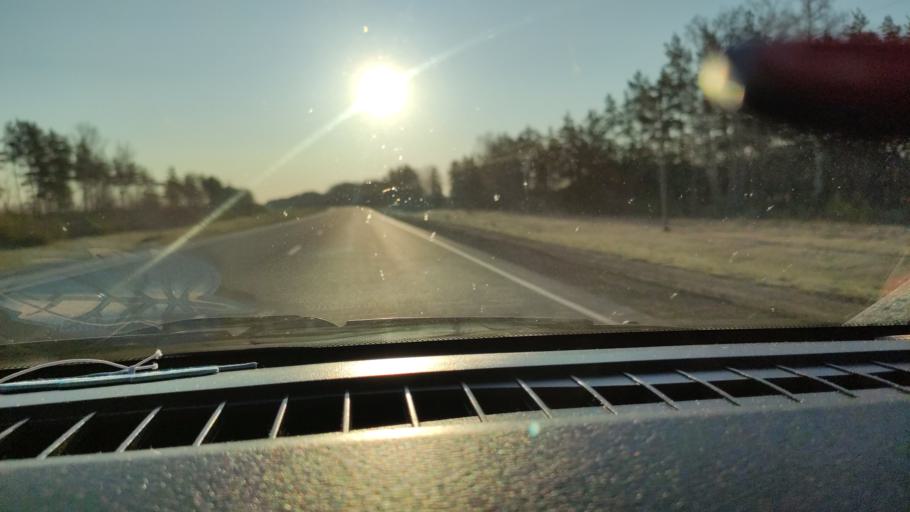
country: RU
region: Saratov
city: Sennoy
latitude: 52.1513
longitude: 46.9956
